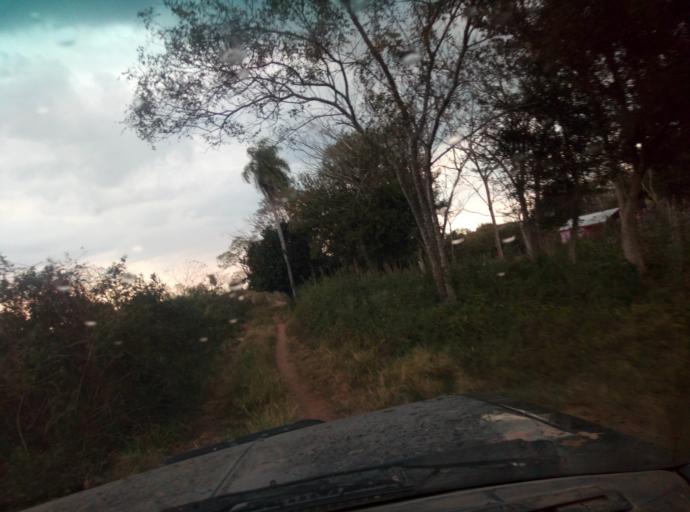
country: PY
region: Caaguazu
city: Doctor Cecilio Baez
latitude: -25.1469
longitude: -56.2231
